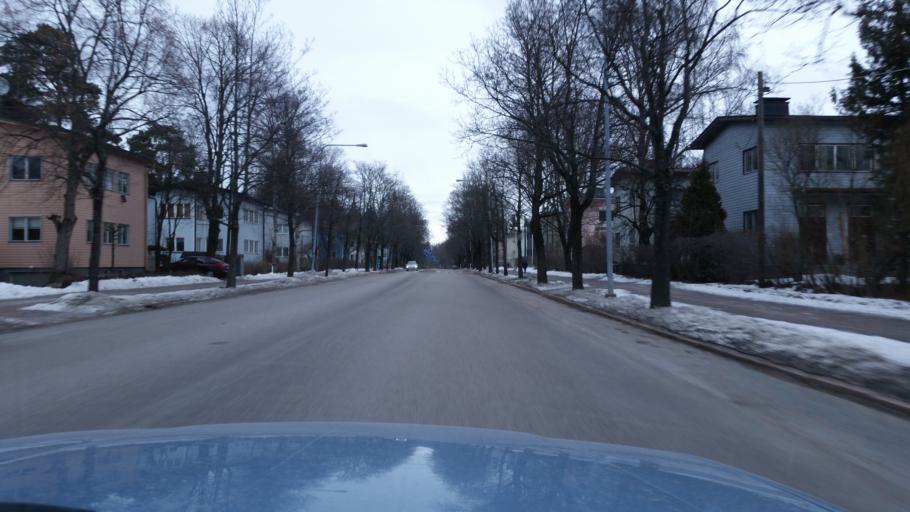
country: FI
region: Uusimaa
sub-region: Helsinki
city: Helsinki
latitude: 60.2207
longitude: 24.9629
